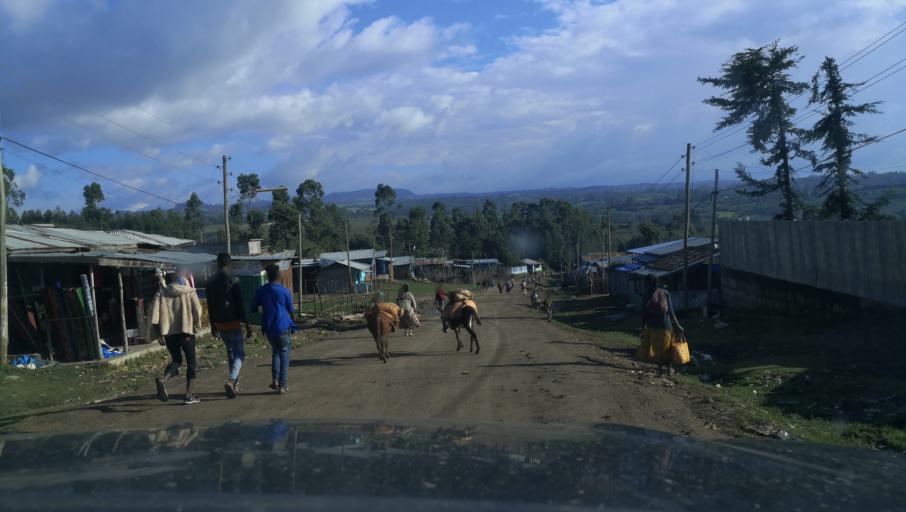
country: ET
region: Oromiya
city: Tulu Bolo
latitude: 8.4614
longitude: 38.2516
